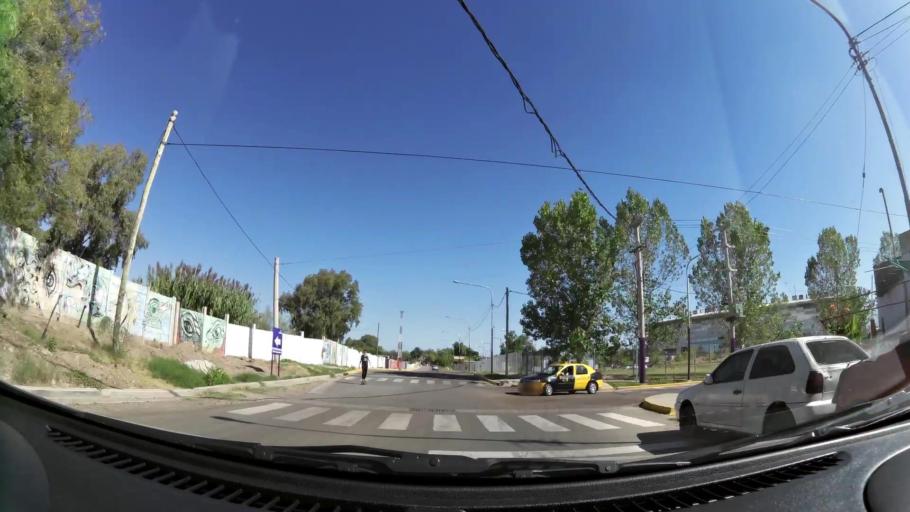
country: AR
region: Mendoza
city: Mendoza
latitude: -32.8862
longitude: -68.8125
